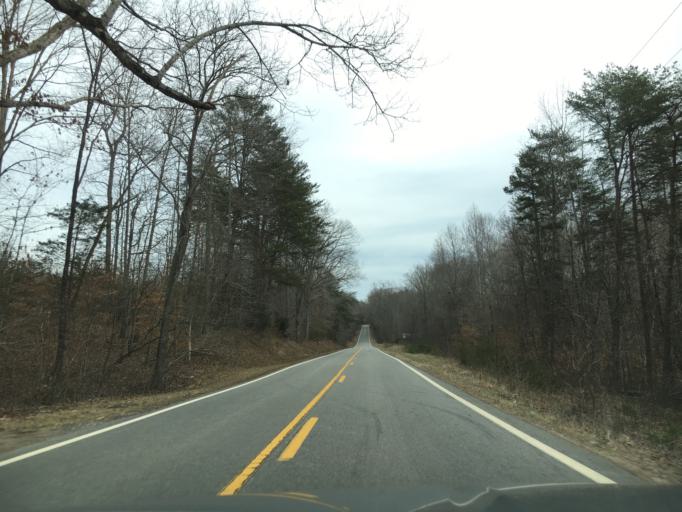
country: US
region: Virginia
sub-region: Charlotte County
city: Charlotte Court House
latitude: 37.1494
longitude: -78.7598
